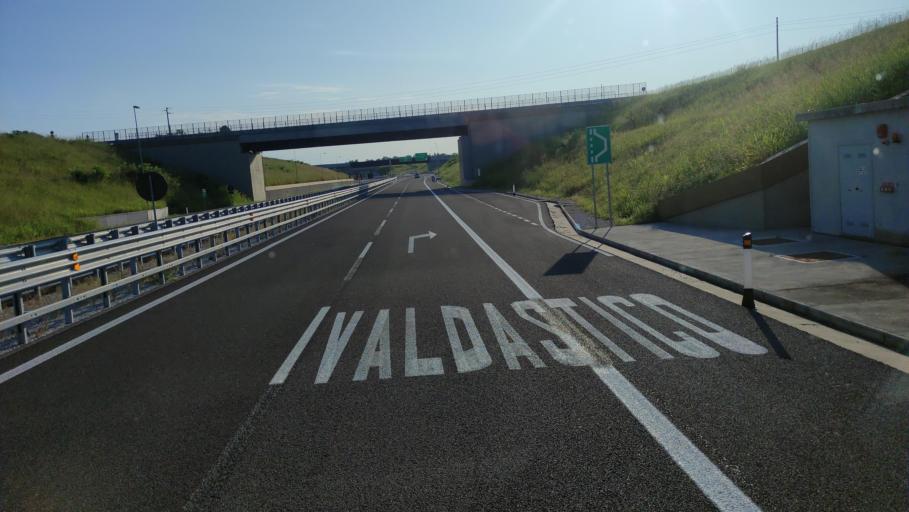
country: IT
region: Veneto
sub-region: Provincia di Vicenza
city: Novoledo
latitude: 45.6653
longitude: 11.5052
